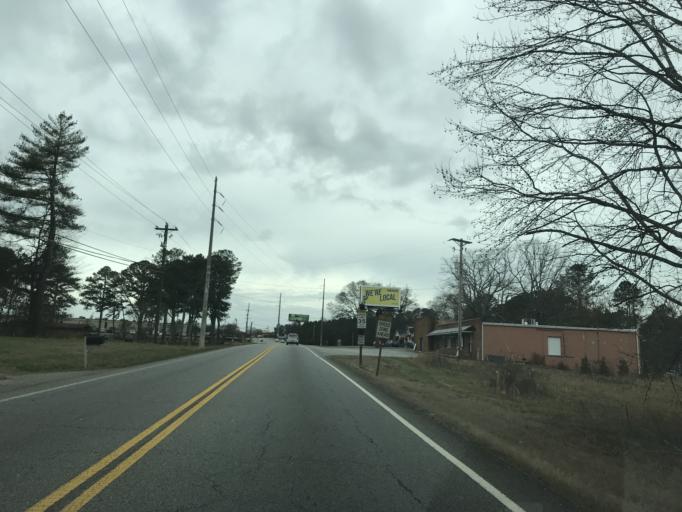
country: US
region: Georgia
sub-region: Fulton County
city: Milton
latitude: 34.1582
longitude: -84.2306
